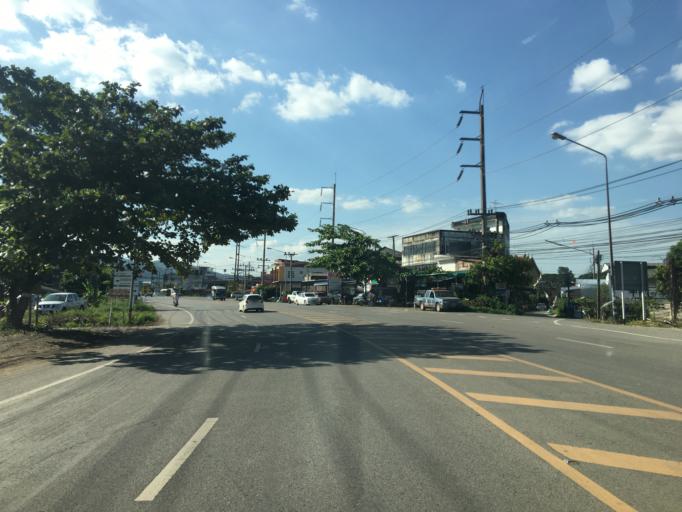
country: TH
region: Phayao
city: Chun
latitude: 19.3387
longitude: 100.1300
